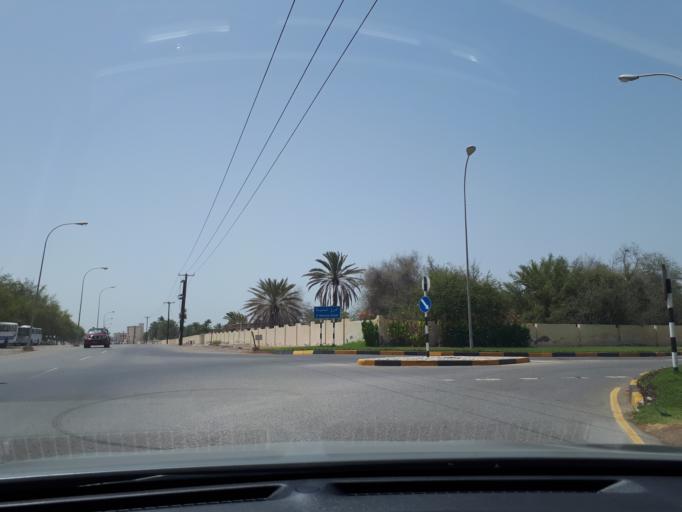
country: OM
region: Muhafazat Masqat
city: As Sib al Jadidah
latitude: 23.6930
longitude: 58.0724
